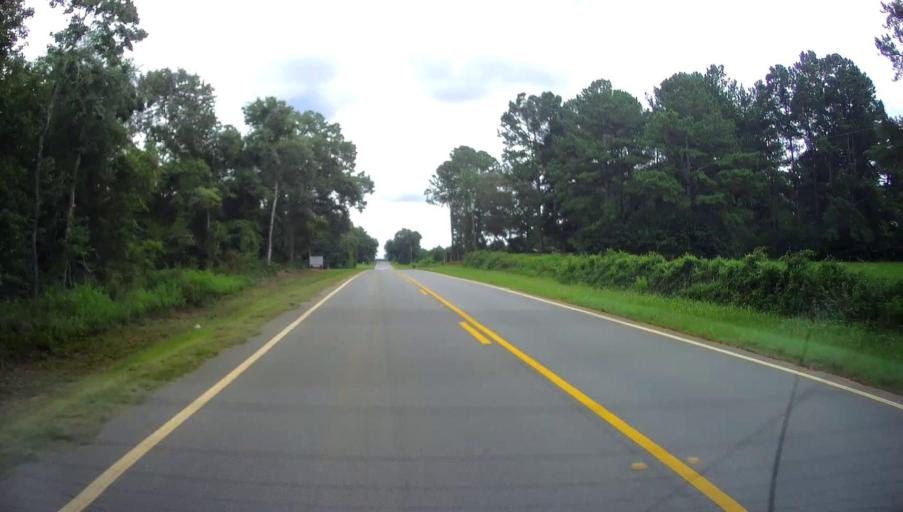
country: US
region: Georgia
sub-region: Macon County
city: Oglethorpe
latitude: 32.2756
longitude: -84.1293
